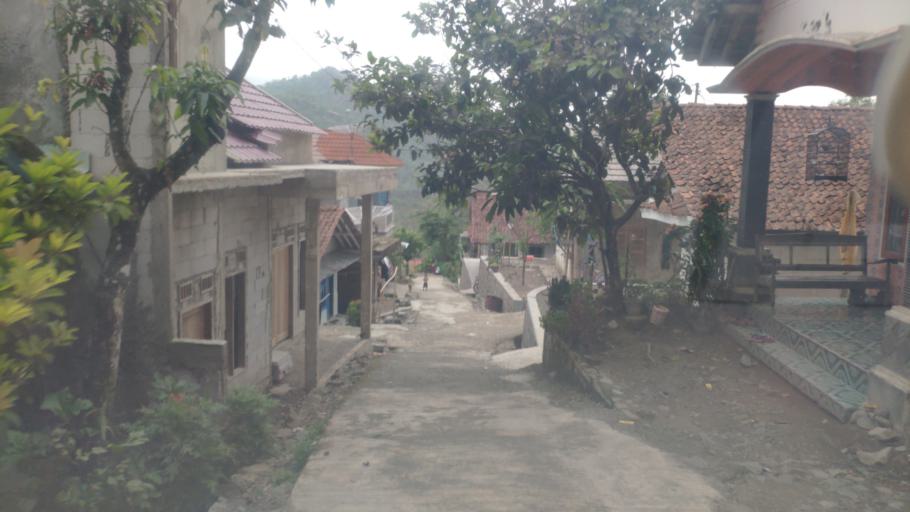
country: ID
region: Central Java
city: Wonosobo
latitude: -7.3057
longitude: 109.7736
